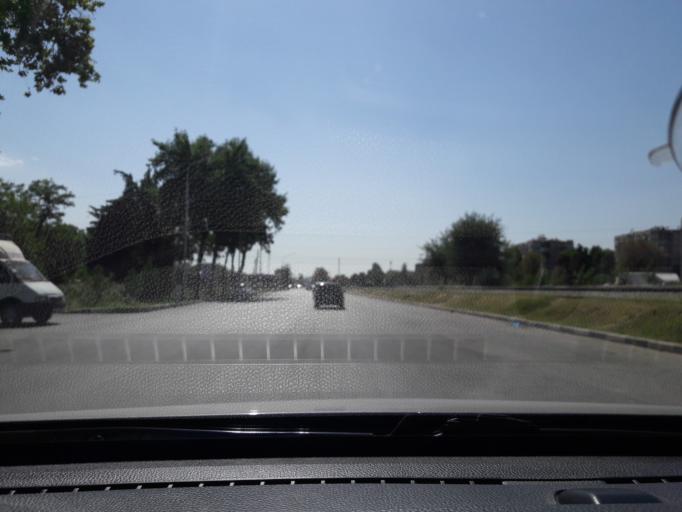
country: TJ
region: Dushanbe
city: Dushanbe
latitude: 38.5679
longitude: 68.7433
